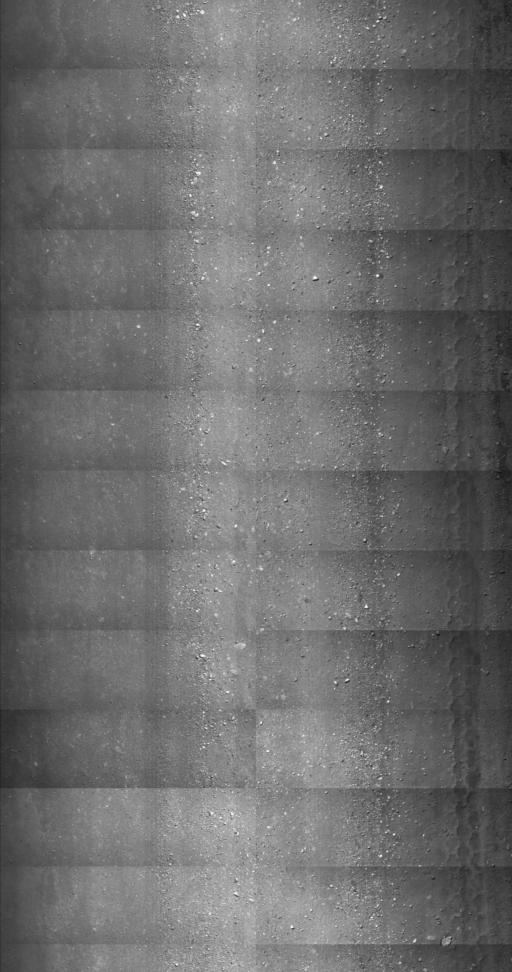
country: US
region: New Hampshire
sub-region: Grafton County
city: Lyme
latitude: 43.8291
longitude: -72.2463
